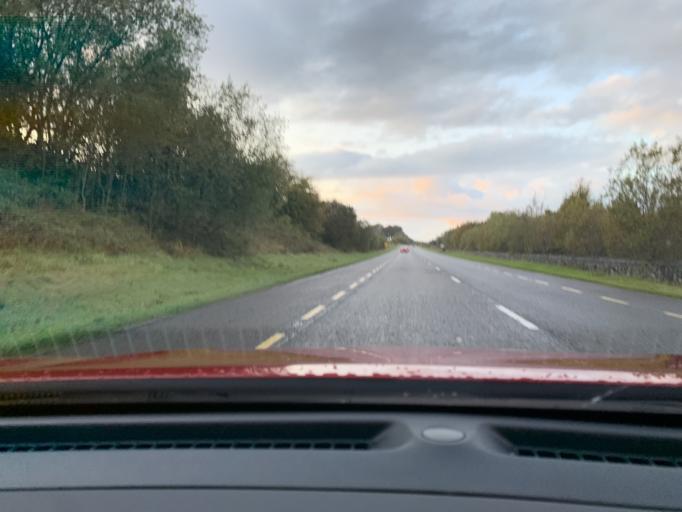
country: IE
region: Connaught
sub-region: Roscommon
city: Boyle
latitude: 54.0613
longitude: -8.3519
